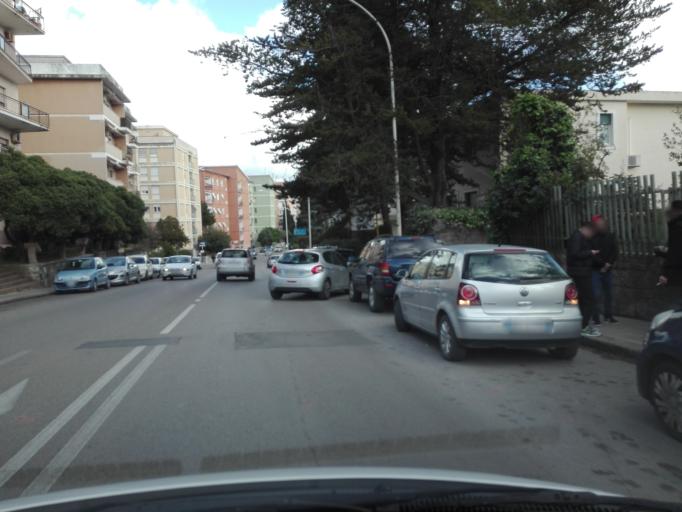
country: IT
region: Sardinia
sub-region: Provincia di Sassari
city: Sassari
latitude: 40.7225
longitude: 8.5766
